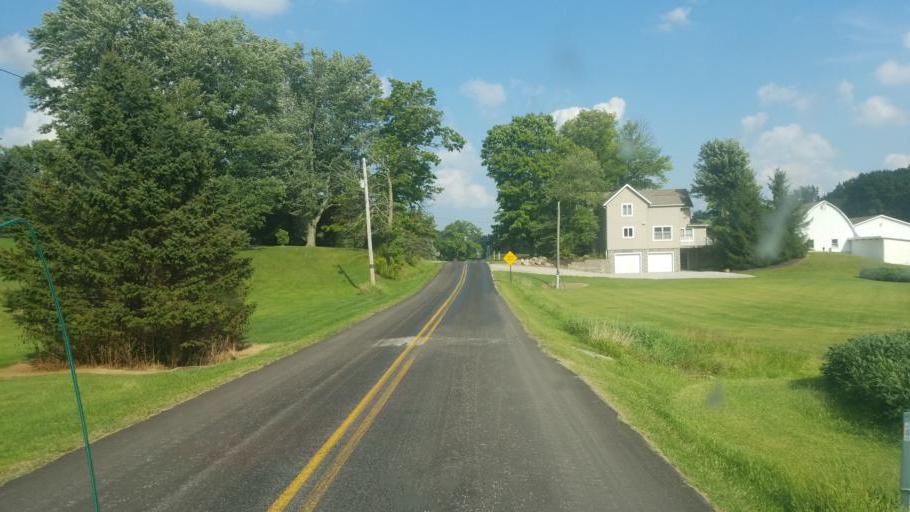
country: US
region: Ohio
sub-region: Medina County
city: Lodi
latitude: 40.9936
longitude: -82.0491
